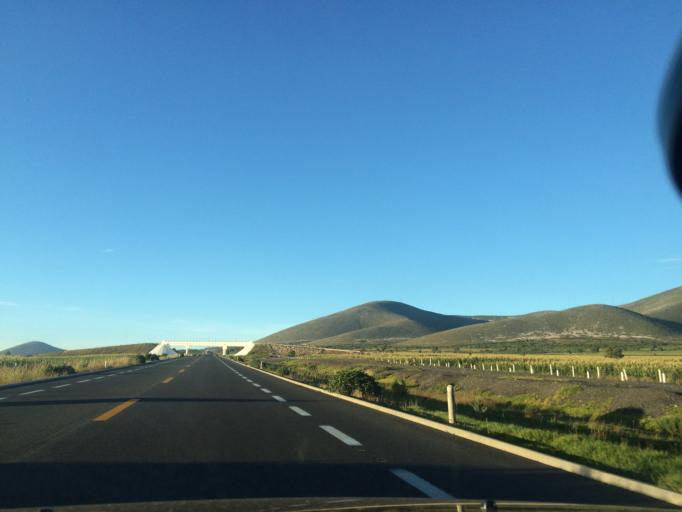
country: MX
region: Puebla
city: Morelos Canada
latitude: 18.7438
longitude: -97.4783
